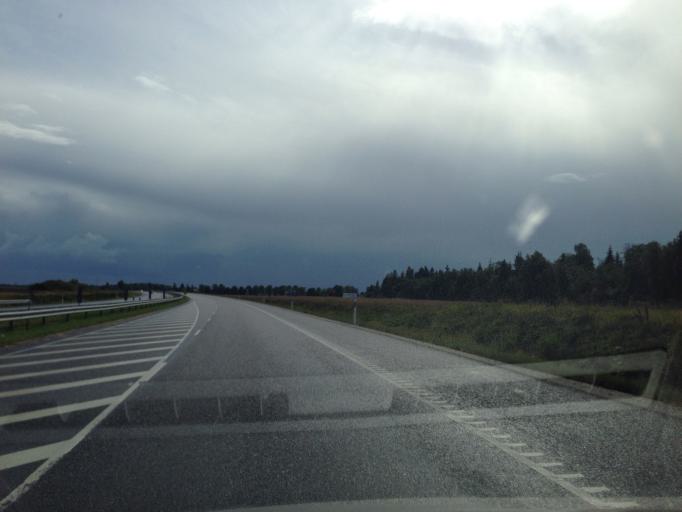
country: EE
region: Jaervamaa
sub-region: Paide linn
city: Paide
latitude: 58.9365
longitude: 25.6102
